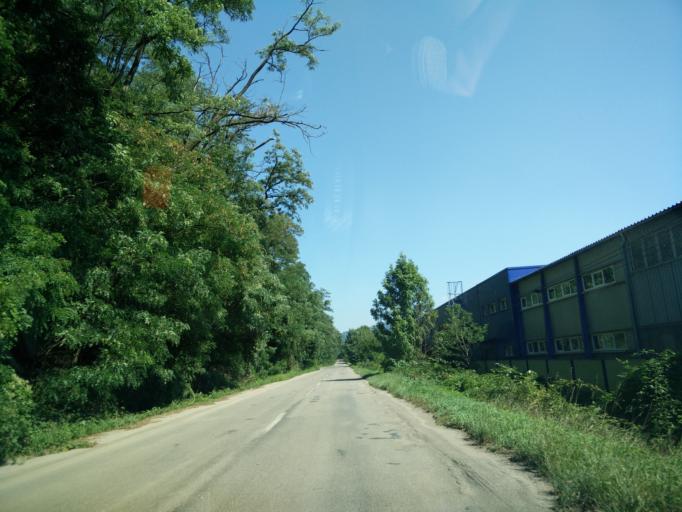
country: SK
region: Banskobystricky
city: Nova Bana
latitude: 48.4186
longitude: 18.6554
